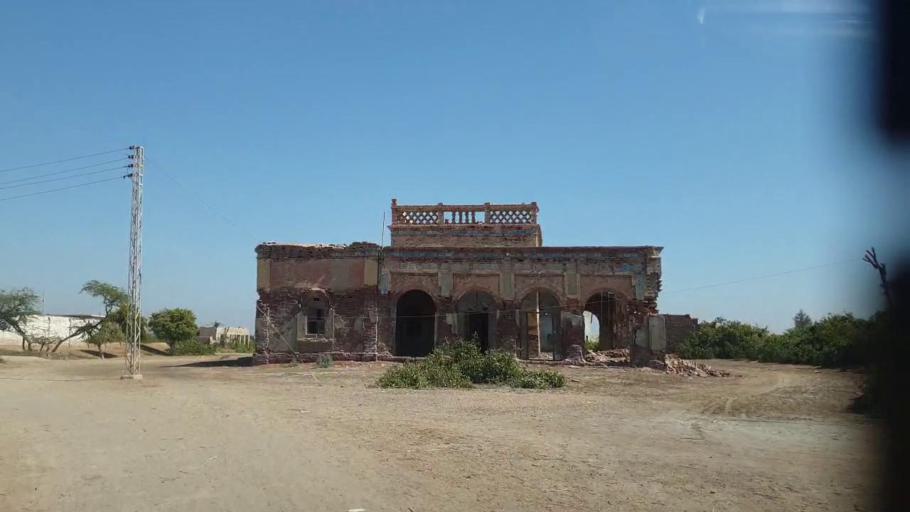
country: PK
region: Sindh
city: Mirpur Khas
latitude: 25.5824
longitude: 69.1154
